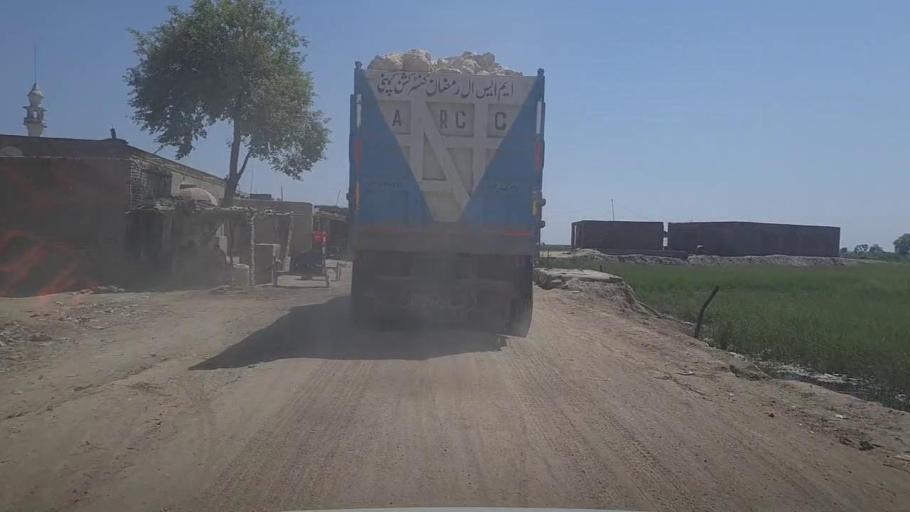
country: PK
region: Sindh
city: Kashmor
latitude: 28.2868
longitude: 69.4356
